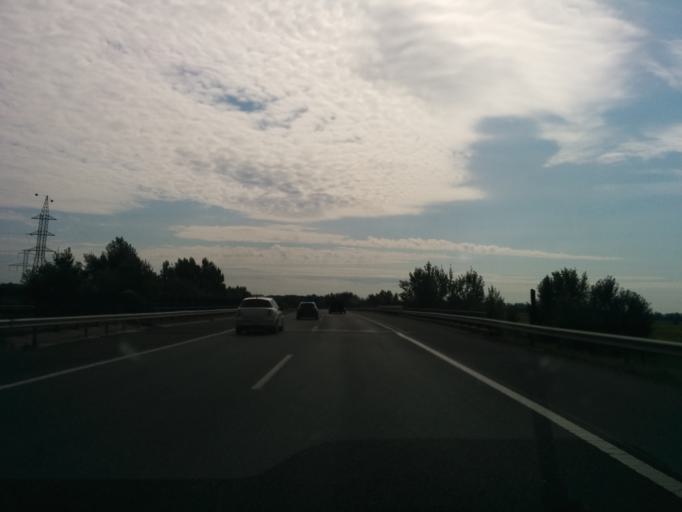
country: HU
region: Gyor-Moson-Sopron
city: Gyor
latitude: 47.6433
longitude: 17.6206
